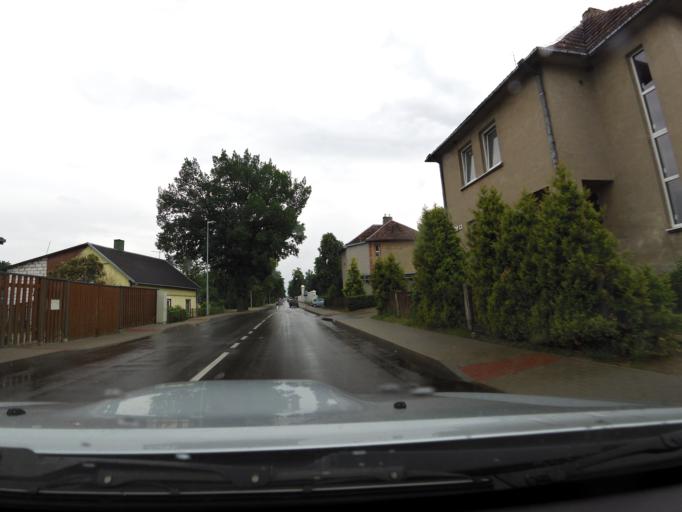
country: LT
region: Marijampoles apskritis
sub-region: Marijampole Municipality
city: Marijampole
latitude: 54.5506
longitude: 23.3458
